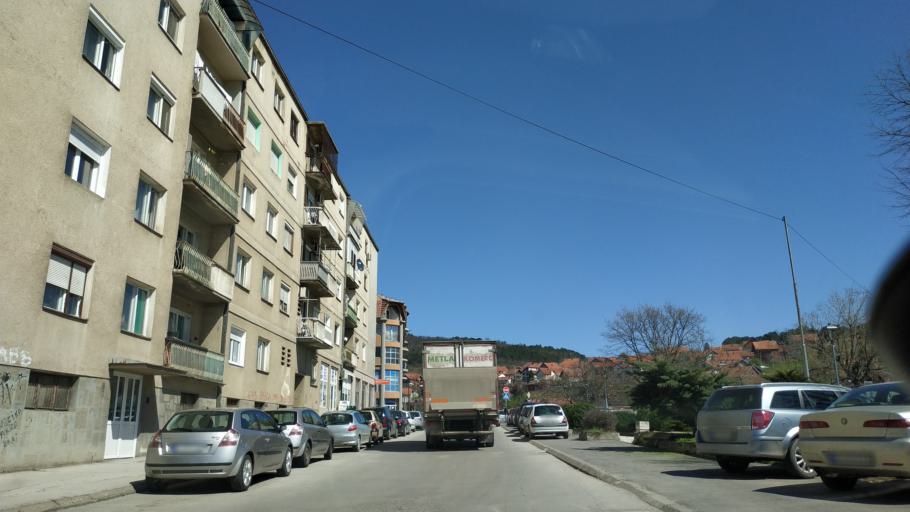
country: RS
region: Central Serbia
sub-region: Nisavski Okrug
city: Aleksinac
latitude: 43.5366
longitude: 21.7094
